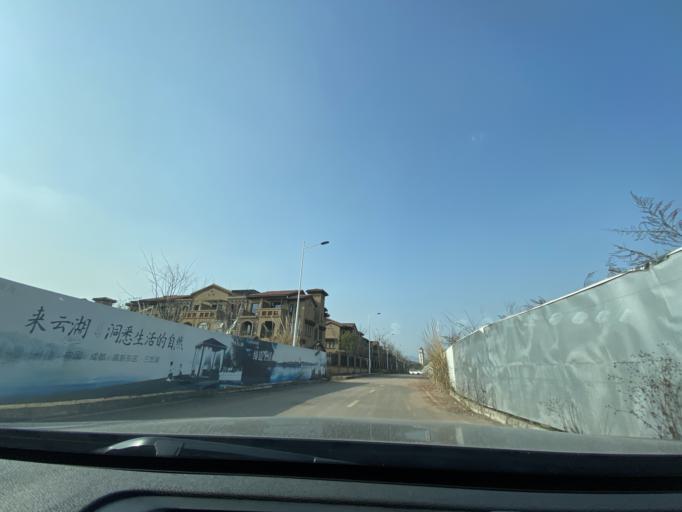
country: CN
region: Sichuan
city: Wenlin
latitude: 30.2524
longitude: 104.2464
